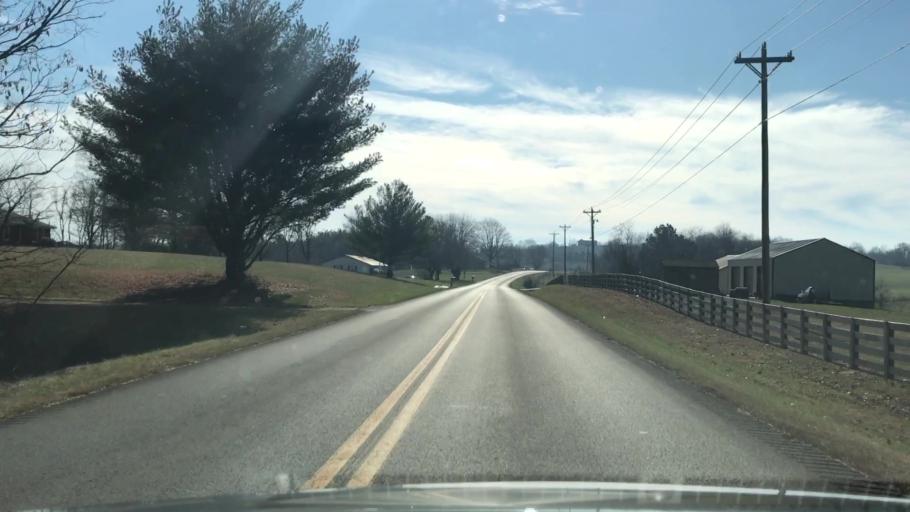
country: US
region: Kentucky
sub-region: Metcalfe County
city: Edmonton
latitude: 36.8911
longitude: -85.6628
